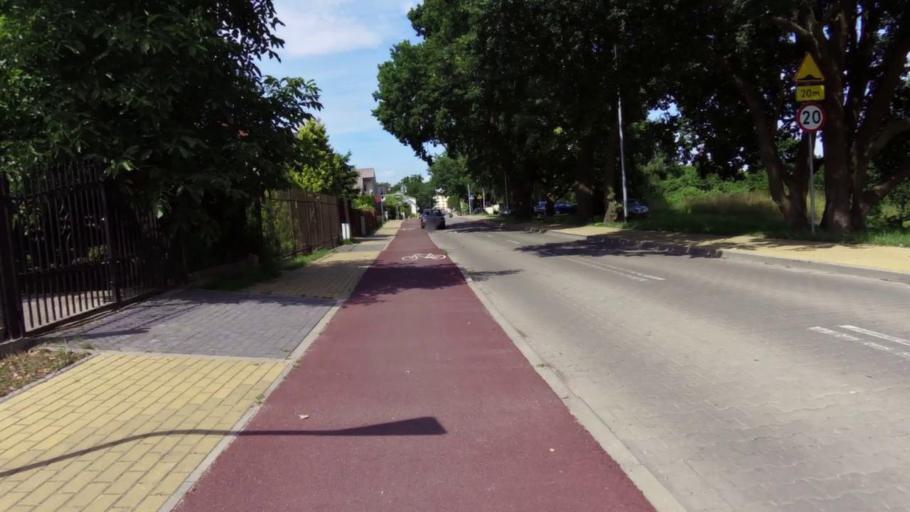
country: PL
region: West Pomeranian Voivodeship
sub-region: Powiat gryfinski
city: Stare Czarnowo
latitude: 53.3718
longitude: 14.6906
